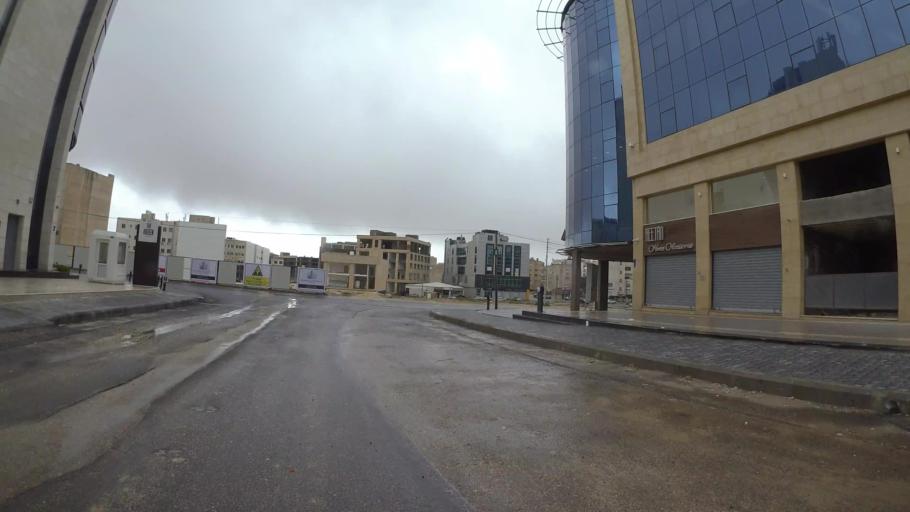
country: JO
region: Amman
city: Wadi as Sir
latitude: 31.9567
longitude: 35.8540
